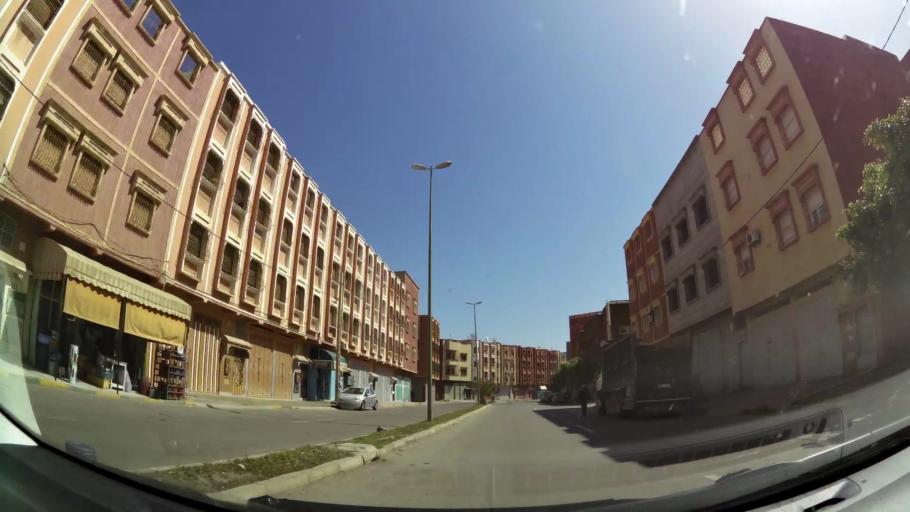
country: MA
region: Souss-Massa-Draa
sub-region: Inezgane-Ait Mellou
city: Inezgane
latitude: 30.3326
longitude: -9.5068
